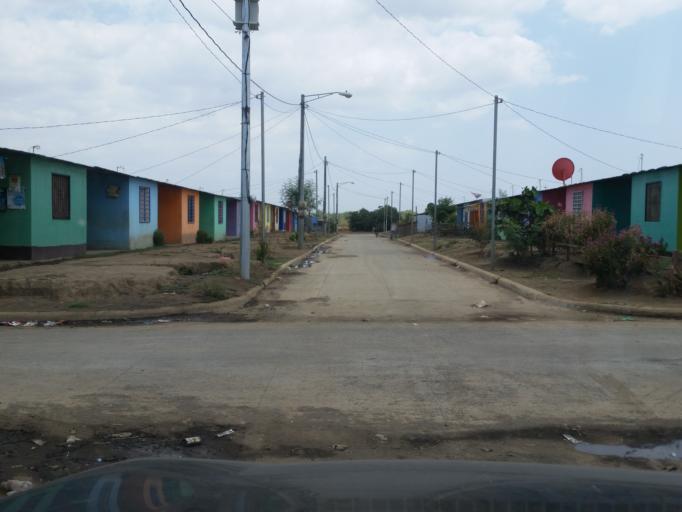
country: NI
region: Managua
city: Managua
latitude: 12.1277
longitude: -86.1581
